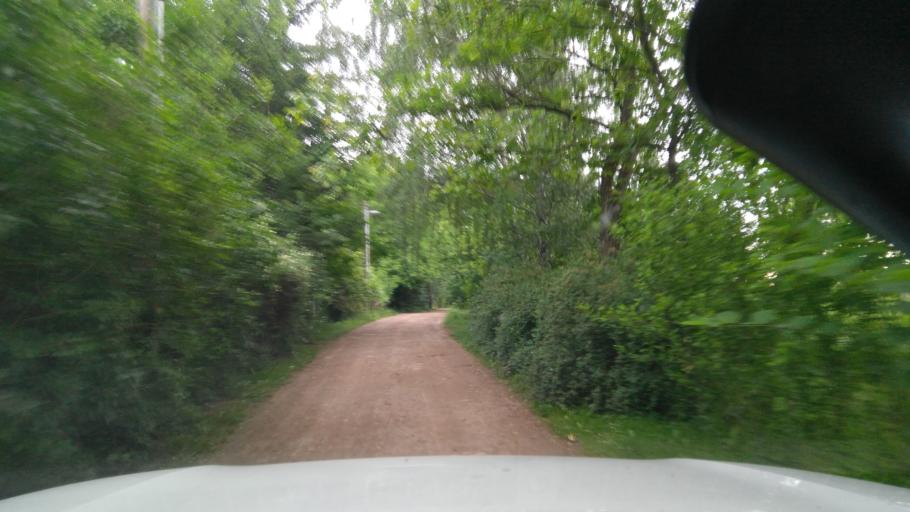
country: HU
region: Bekes
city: Bekescsaba
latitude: 46.6726
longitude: 21.1810
